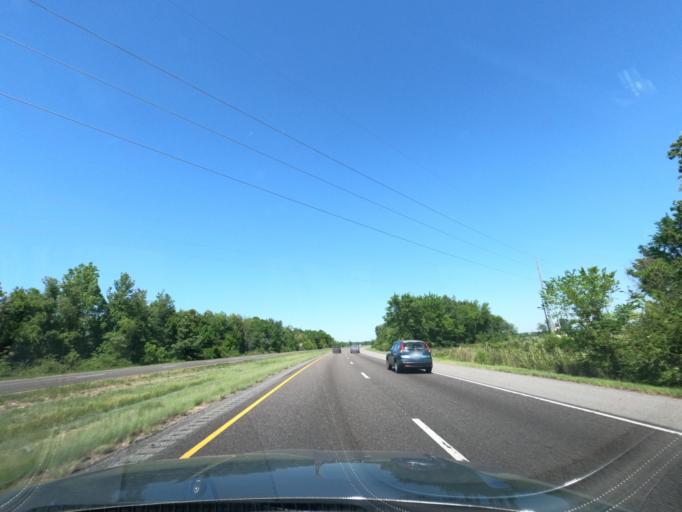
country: US
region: Georgia
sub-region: Richmond County
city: Augusta
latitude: 33.4274
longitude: -81.9588
